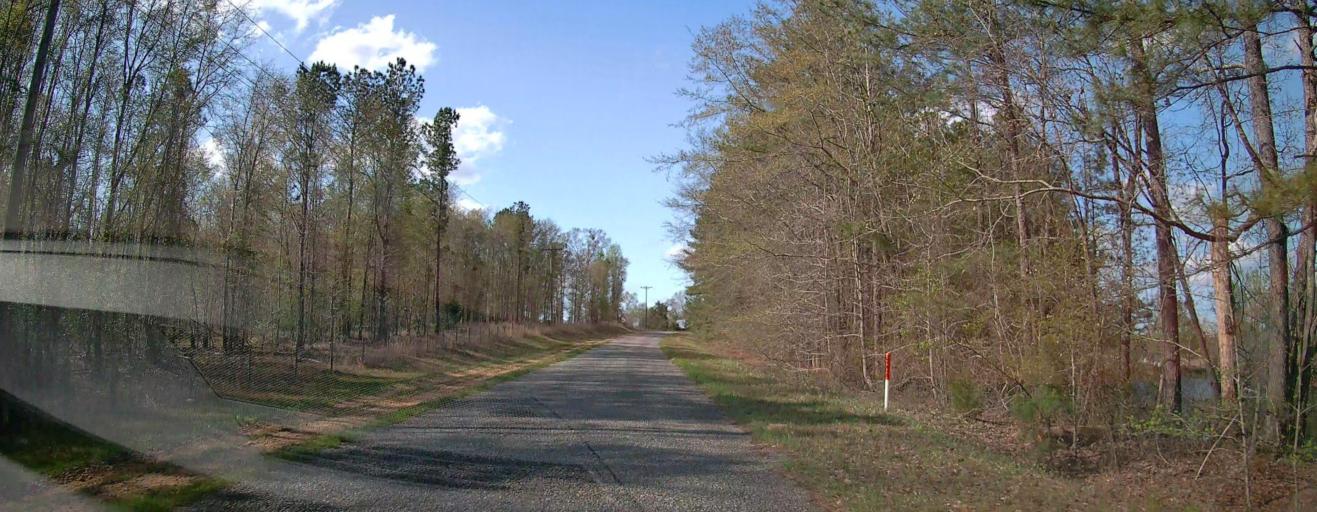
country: US
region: Georgia
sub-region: Baldwin County
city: Hardwick
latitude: 33.0271
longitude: -83.1186
